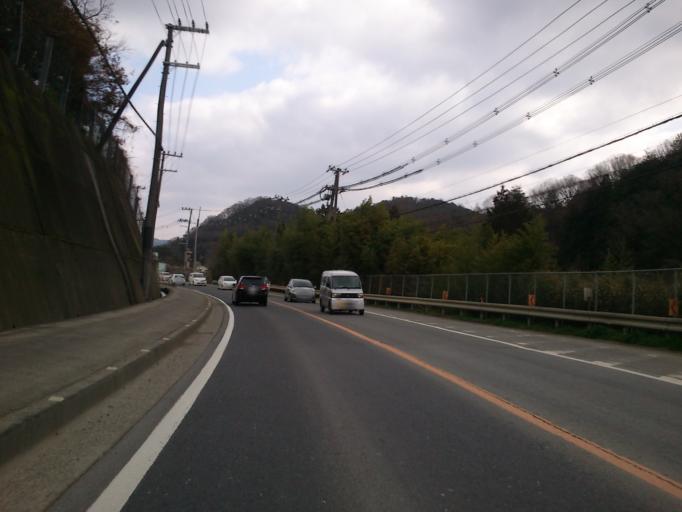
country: JP
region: Kyoto
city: Tanabe
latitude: 34.8337
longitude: 135.8244
